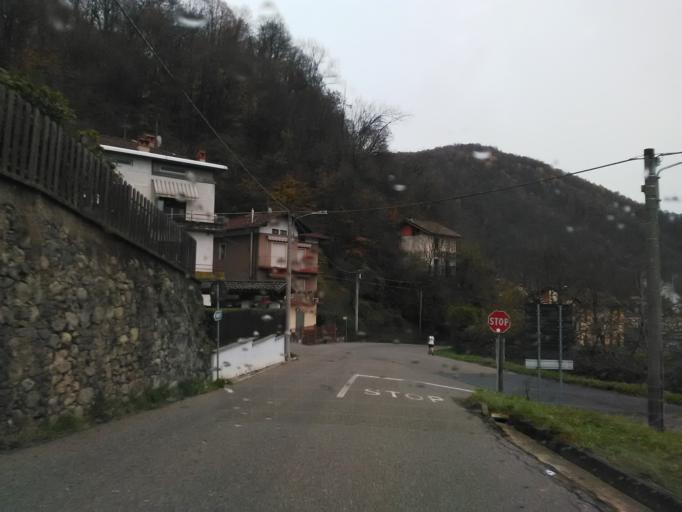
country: IT
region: Piedmont
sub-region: Provincia di Biella
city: Pray
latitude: 45.6762
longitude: 8.2168
